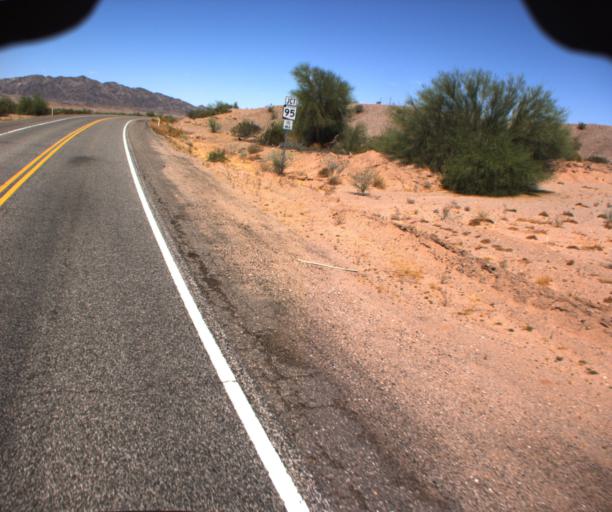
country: US
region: Arizona
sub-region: La Paz County
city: Parker
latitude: 33.9930
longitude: -114.2080
